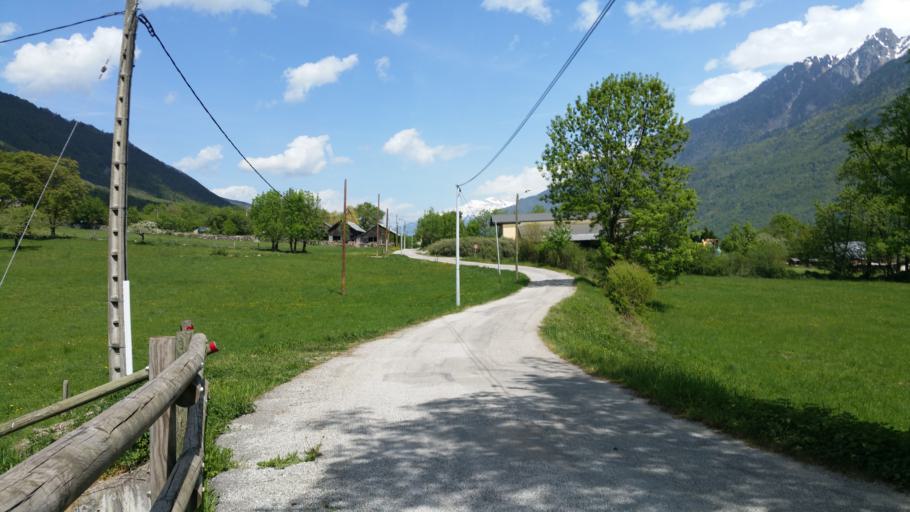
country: FR
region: Rhone-Alpes
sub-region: Departement de la Savoie
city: Saint-Remy-de-Maurienne
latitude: 45.3866
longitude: 6.2624
